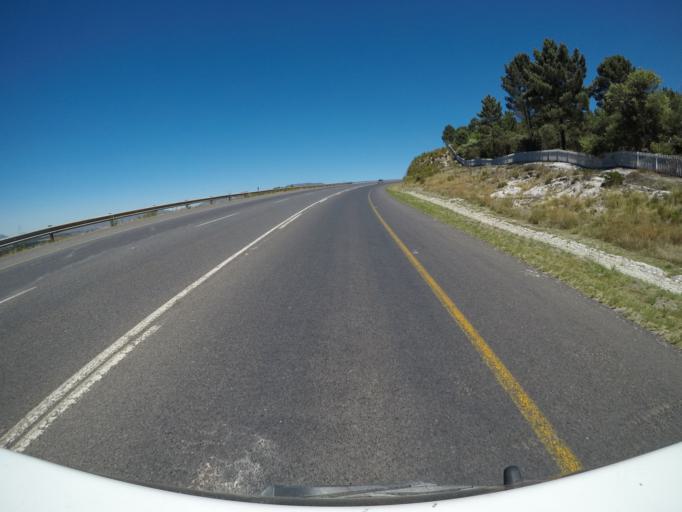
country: ZA
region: Western Cape
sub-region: Overberg District Municipality
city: Grabouw
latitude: -34.1664
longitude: 19.0013
